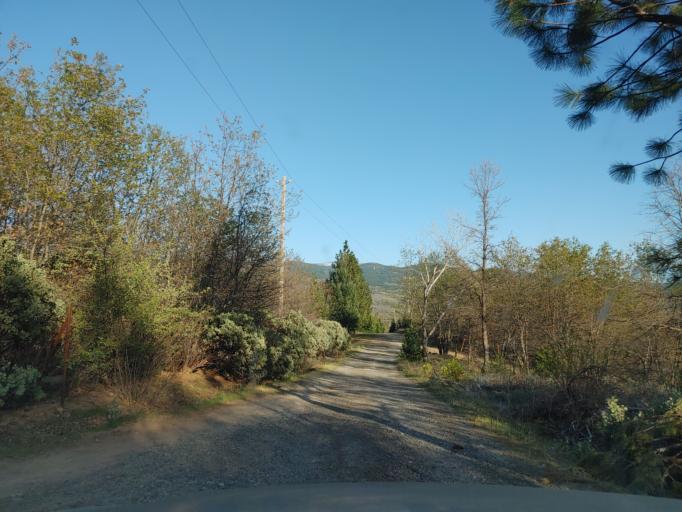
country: US
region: California
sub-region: Shasta County
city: Burney
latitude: 40.8112
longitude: -121.9447
